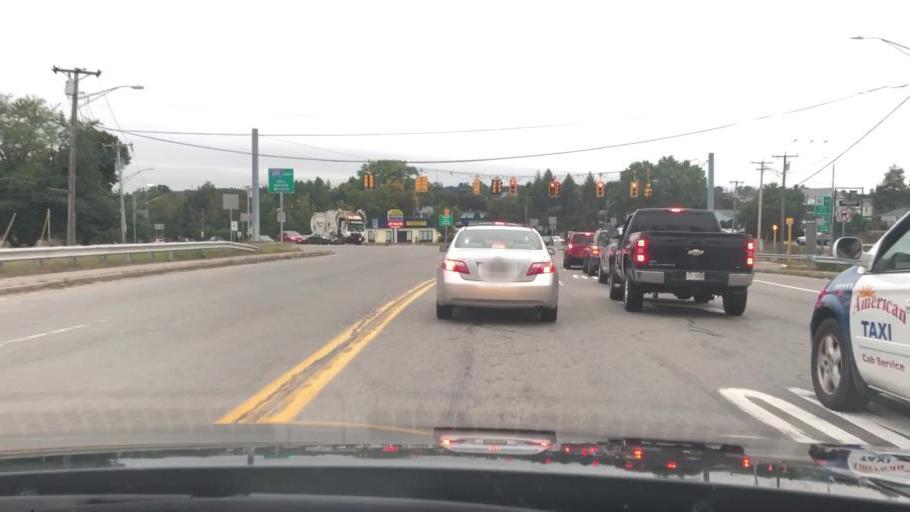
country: US
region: Massachusetts
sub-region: Essex County
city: North Andover
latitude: 42.7274
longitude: -71.1397
